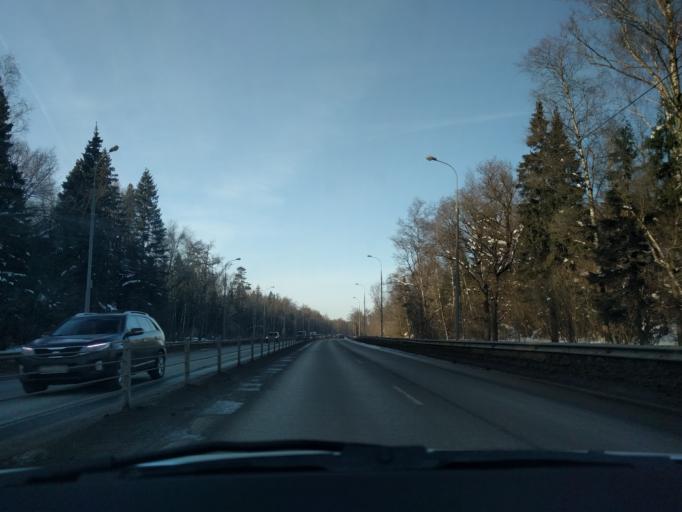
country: RU
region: Moskovskaya
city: Marfino
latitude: 56.0270
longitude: 37.5431
